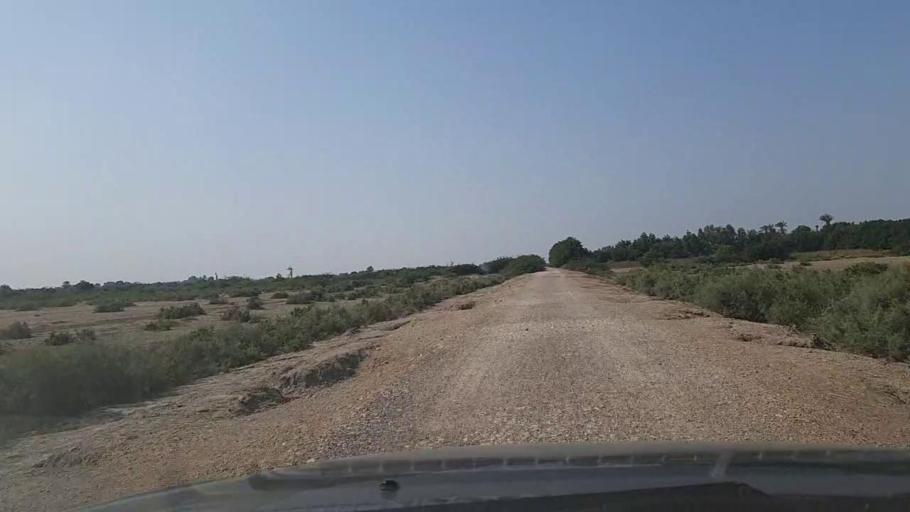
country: PK
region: Sindh
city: Mirpur Sakro
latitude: 24.4060
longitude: 67.6793
